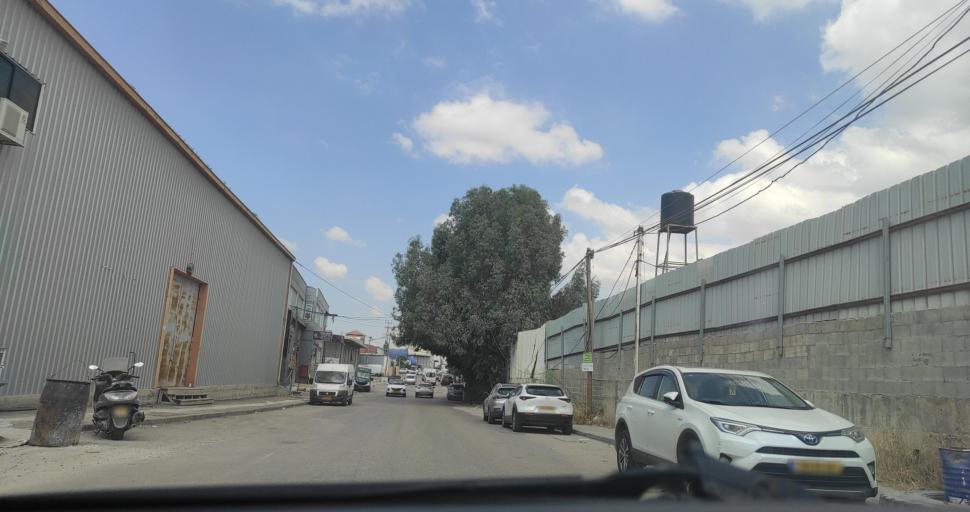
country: IL
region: Central District
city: Rosh Ha'Ayin
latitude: 32.1145
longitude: 34.9560
